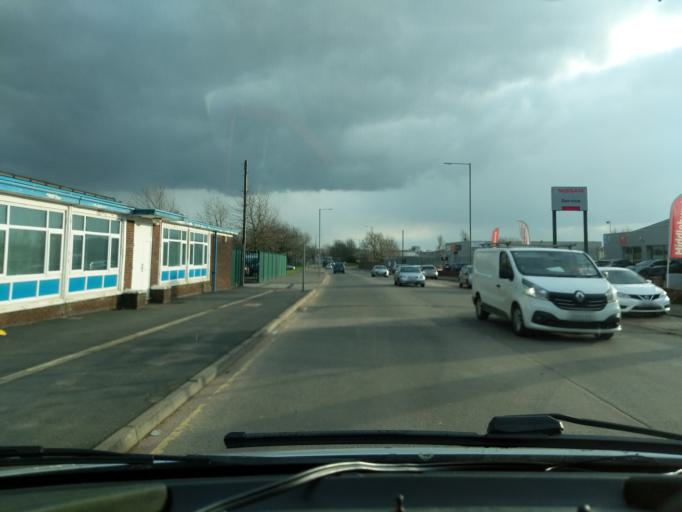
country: GB
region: England
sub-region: St. Helens
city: St Helens
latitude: 53.4510
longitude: -2.7226
